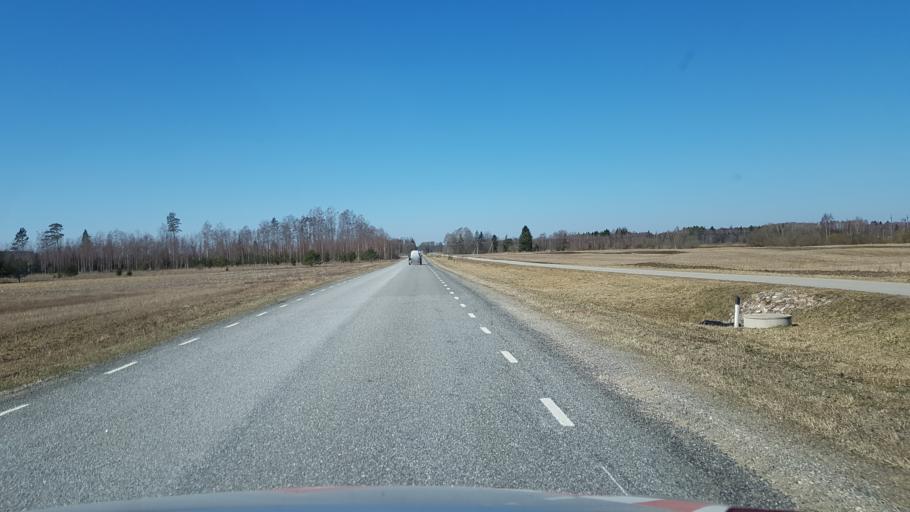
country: EE
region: Laeaene-Virumaa
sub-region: Rakke vald
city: Rakke
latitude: 58.9950
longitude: 26.2181
